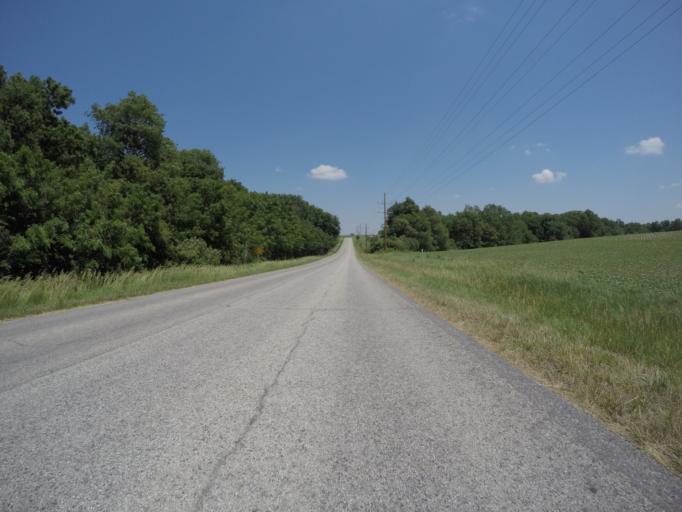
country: US
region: Kansas
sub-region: Doniphan County
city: Troy
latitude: 39.7643
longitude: -95.1323
